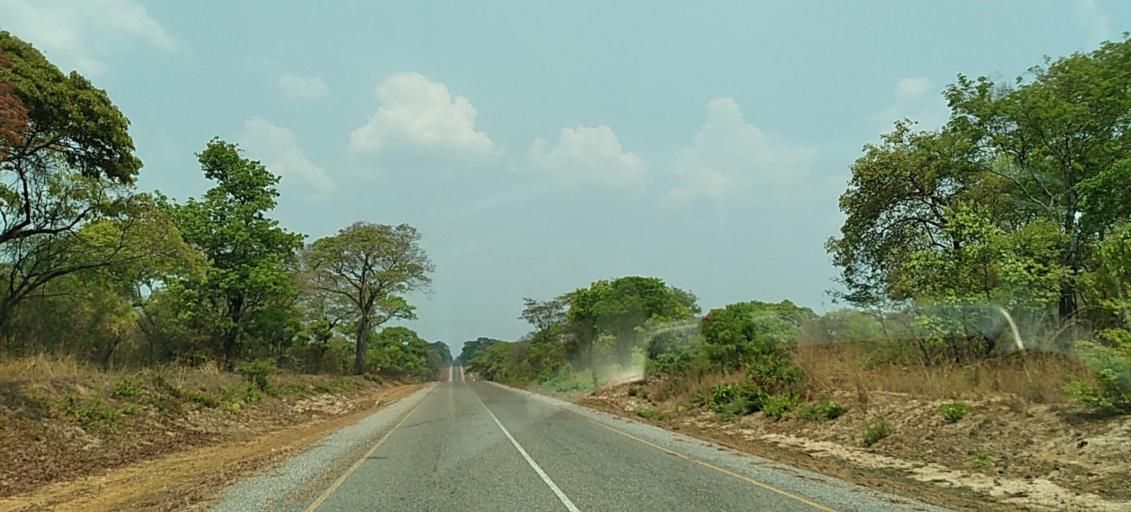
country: ZM
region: North-Western
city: Zambezi
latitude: -13.5659
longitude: 23.2219
